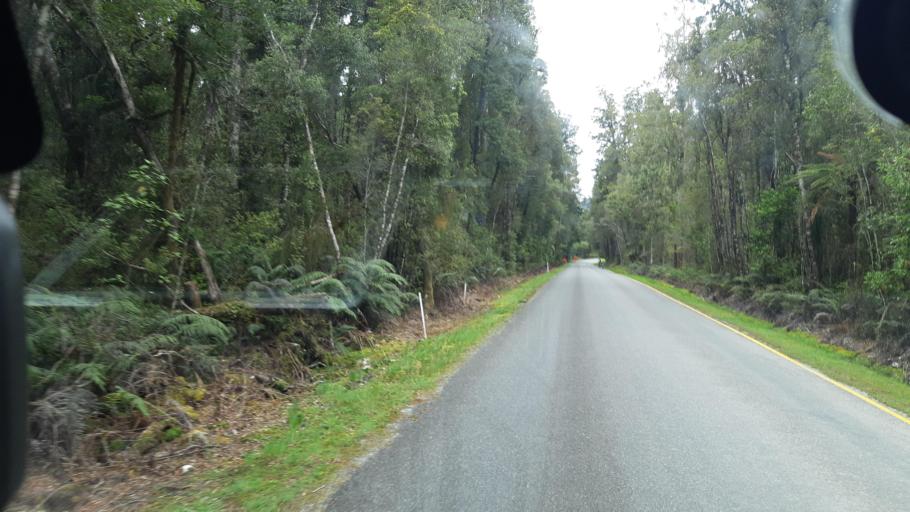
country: NZ
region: West Coast
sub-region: Westland District
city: Hokitika
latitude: -42.7997
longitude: 171.1480
